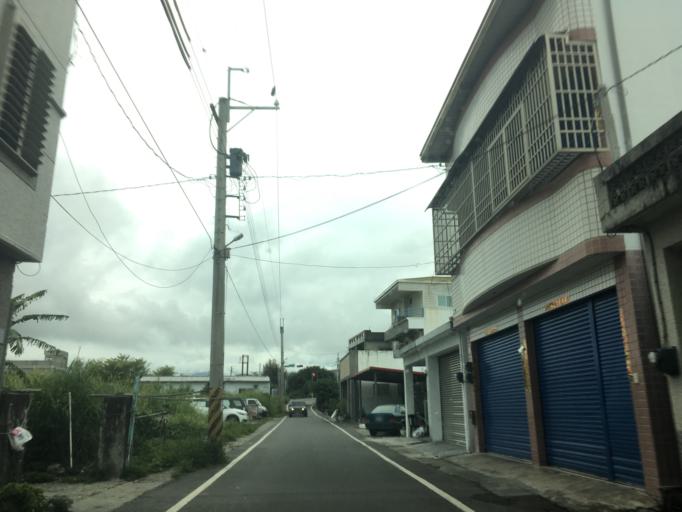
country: TW
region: Taiwan
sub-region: Taitung
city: Taitung
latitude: 22.7933
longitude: 121.1890
